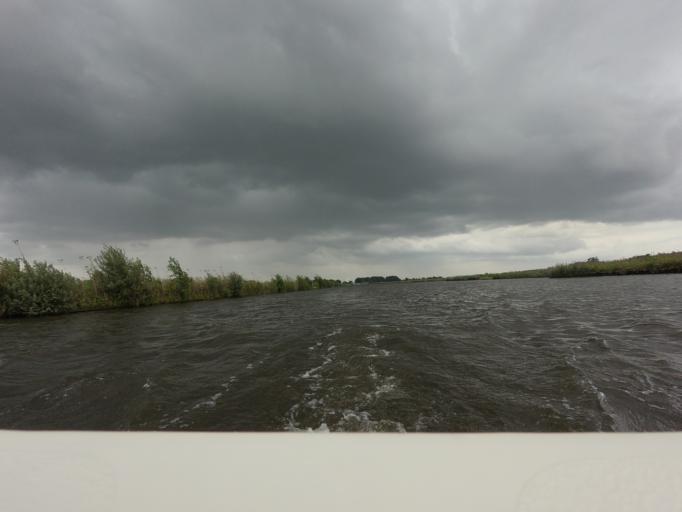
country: NL
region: Friesland
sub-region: Gemeente Smallingerland
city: Oudega
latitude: 53.1141
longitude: 5.9467
